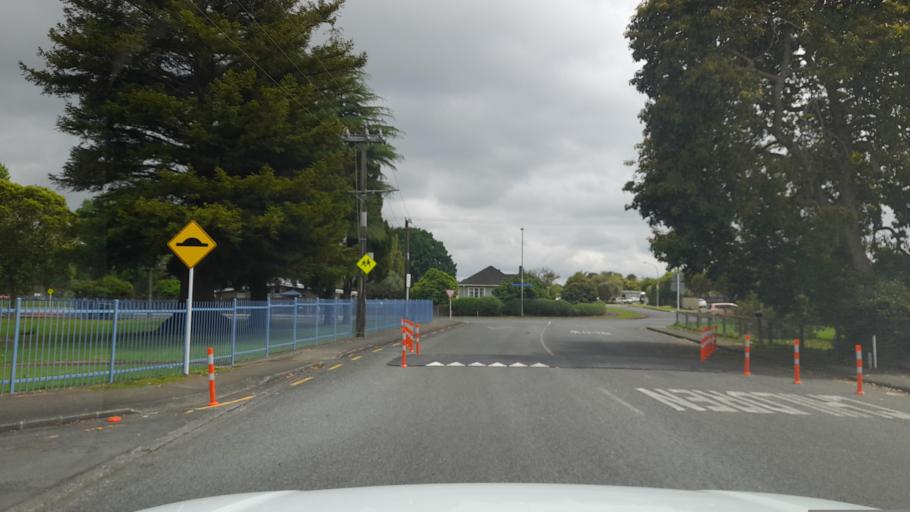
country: NZ
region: Northland
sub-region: Far North District
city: Waimate North
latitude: -35.4089
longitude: 173.8058
